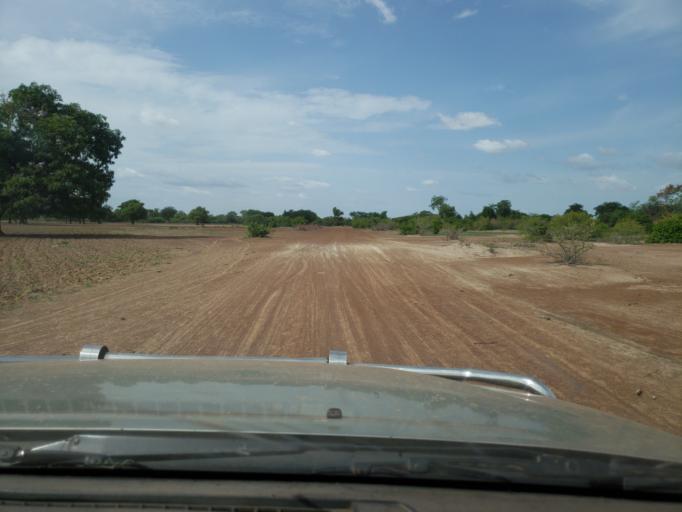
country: ML
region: Segou
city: Bla
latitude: 12.7545
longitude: -5.6297
